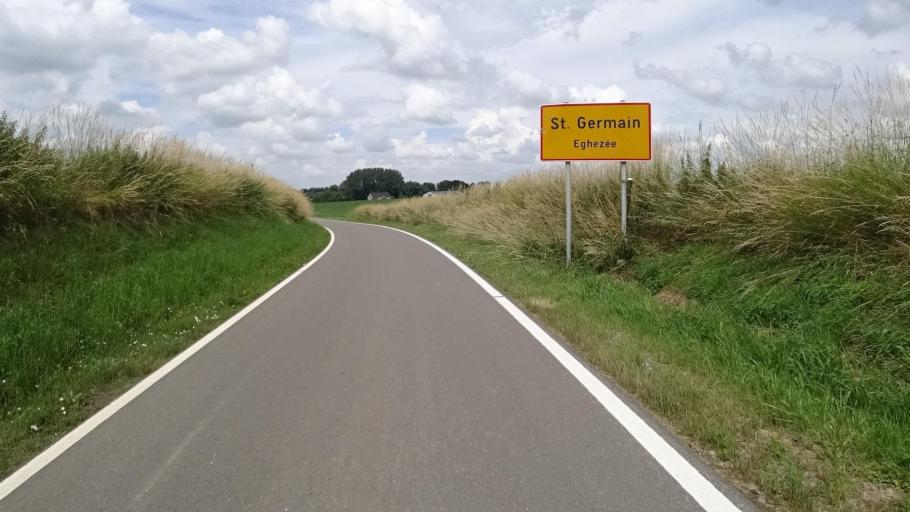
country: BE
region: Wallonia
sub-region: Province du Brabant Wallon
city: Perwez
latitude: 50.5540
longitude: 4.8330
